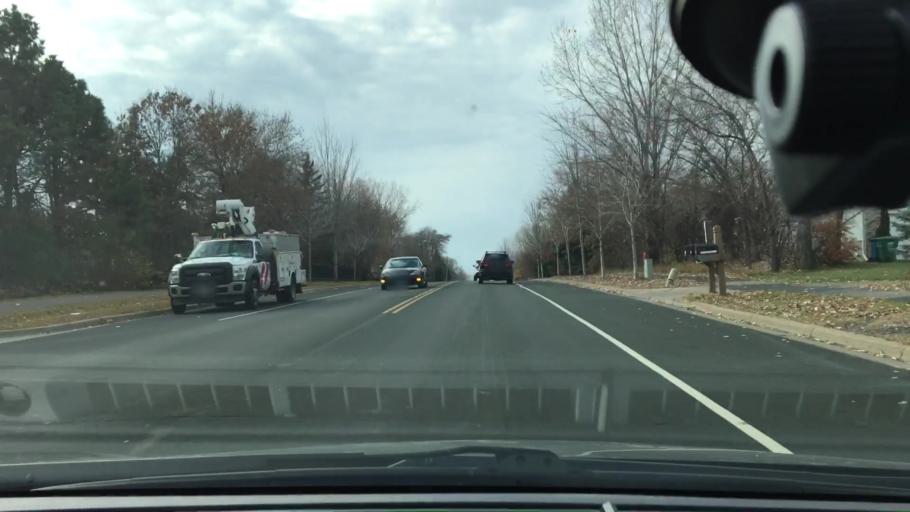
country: US
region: Minnesota
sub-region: Hennepin County
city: Corcoran
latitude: 45.1167
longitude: -93.5040
